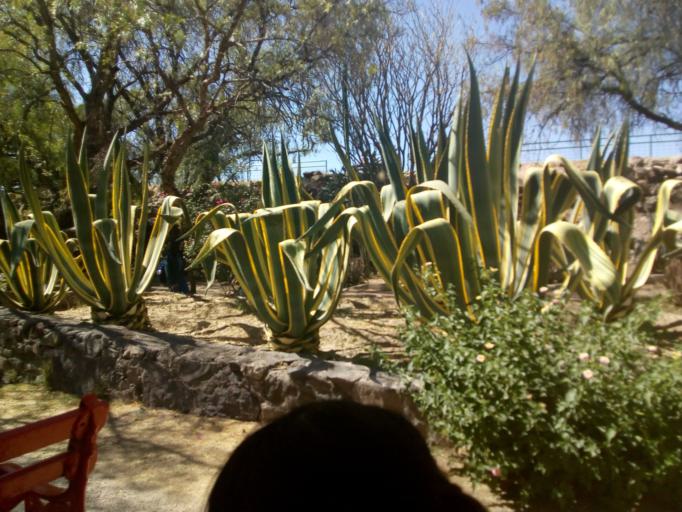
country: MX
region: Guanajuato
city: Leon
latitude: 21.1731
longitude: -101.6794
